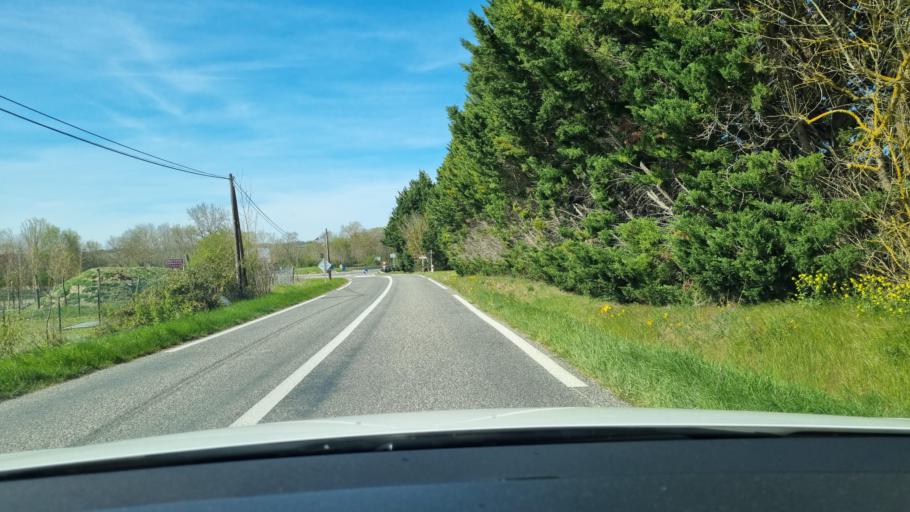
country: FR
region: Midi-Pyrenees
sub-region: Departement du Gers
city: Samatan
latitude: 43.4955
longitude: 0.9693
